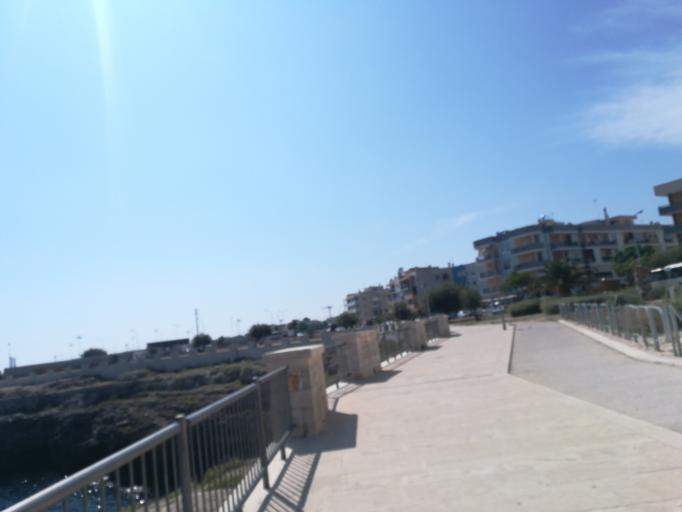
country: IT
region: Apulia
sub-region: Provincia di Bari
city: Polignano a Mare
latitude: 40.9941
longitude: 17.2290
